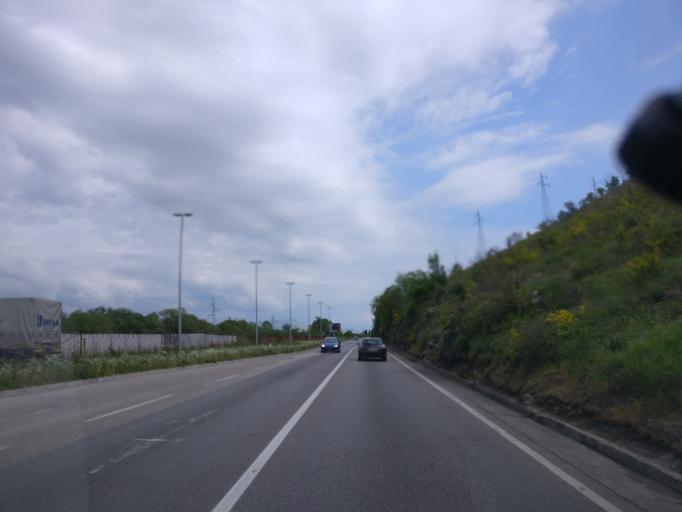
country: ME
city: Spuz
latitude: 42.4521
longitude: 19.1963
